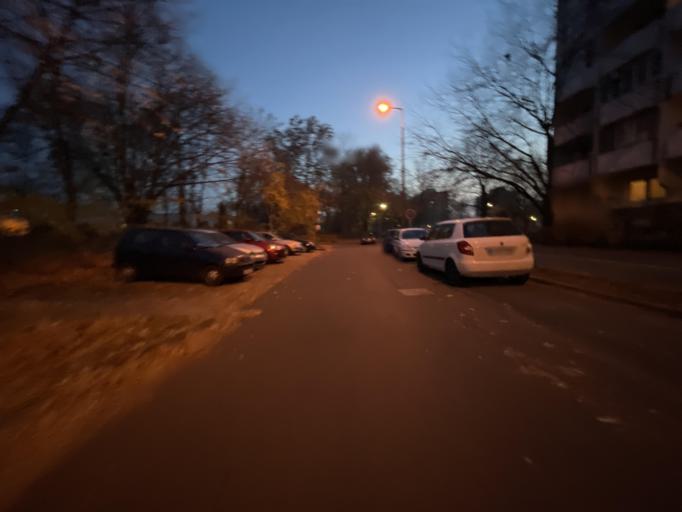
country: HU
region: Hajdu-Bihar
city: Debrecen
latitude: 47.5211
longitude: 21.6014
